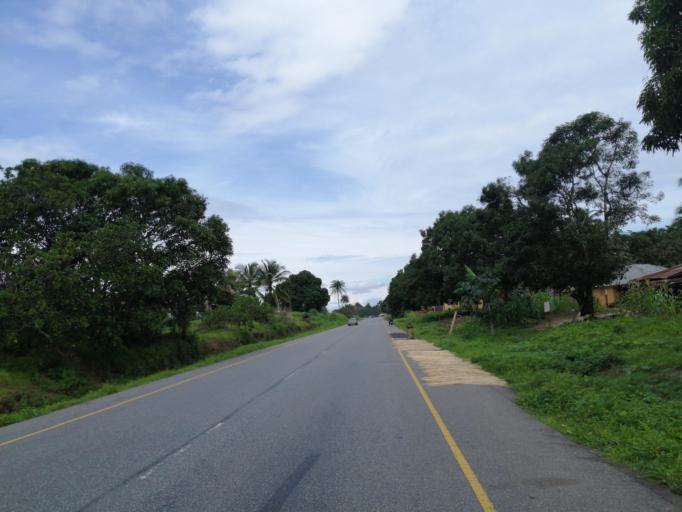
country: SL
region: Northern Province
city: Port Loko
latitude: 8.7443
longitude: -12.9308
